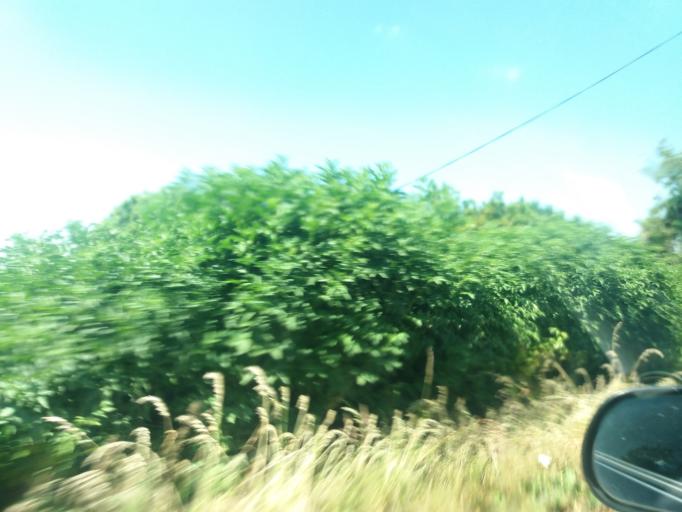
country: IE
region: Leinster
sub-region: An Mhi
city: Stamullin
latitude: 53.5708
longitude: -6.3140
